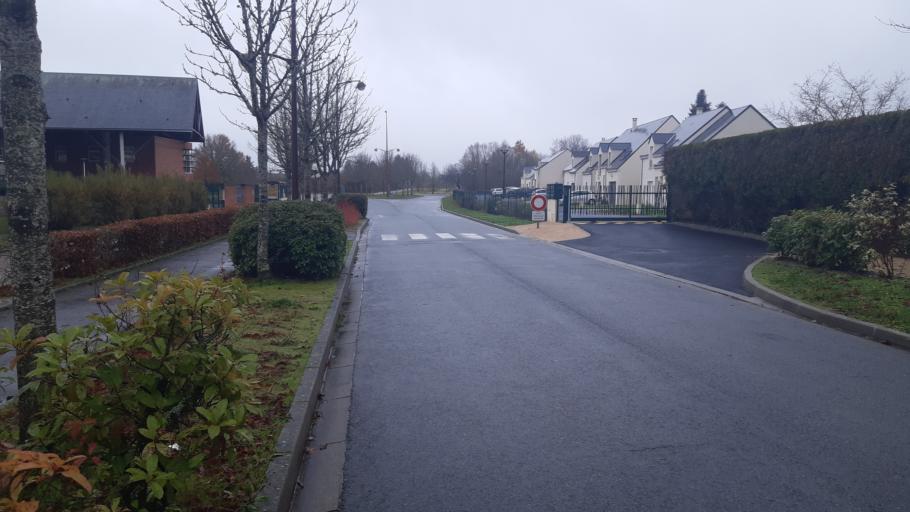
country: FR
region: Centre
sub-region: Departement du Loiret
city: Olivet
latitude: 47.8660
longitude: 1.8862
